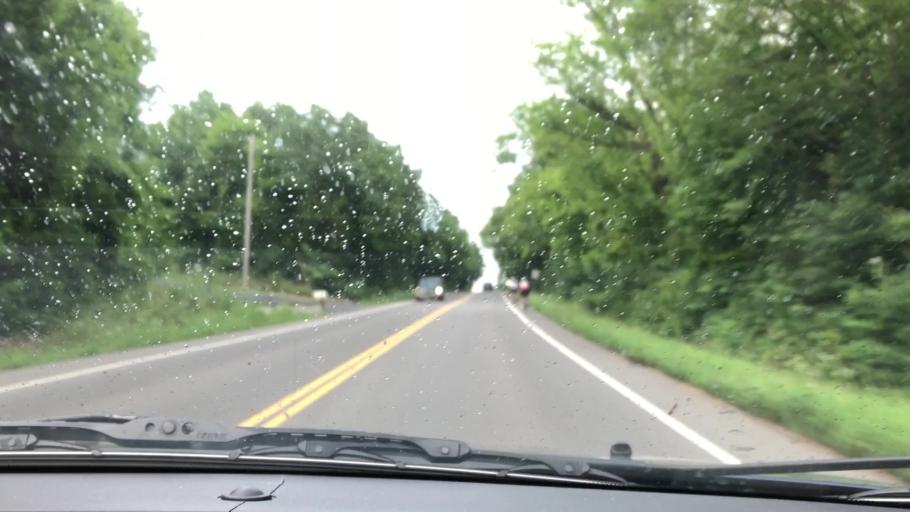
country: US
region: Tennessee
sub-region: Williamson County
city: Franklin
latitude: 35.8974
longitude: -86.9169
